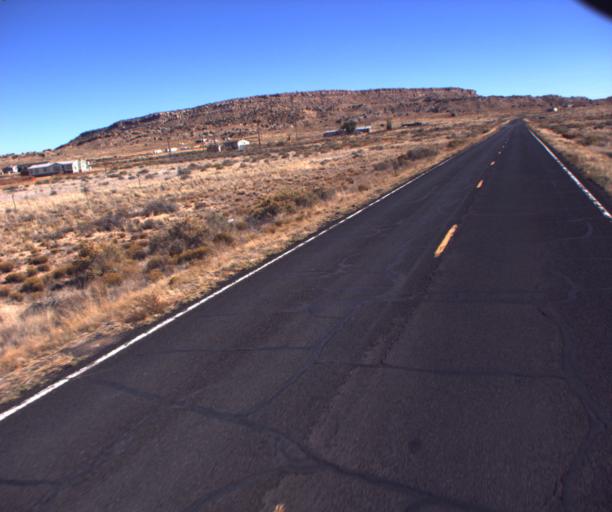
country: US
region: Arizona
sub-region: Navajo County
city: First Mesa
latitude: 35.8397
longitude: -110.3111
